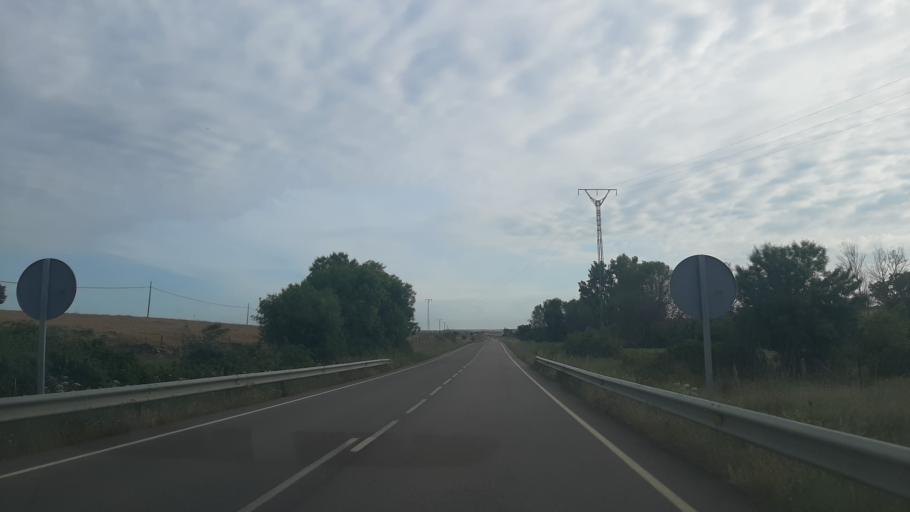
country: ES
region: Castille and Leon
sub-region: Provincia de Salamanca
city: Gallegos de Arganan
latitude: 40.6095
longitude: -6.7067
